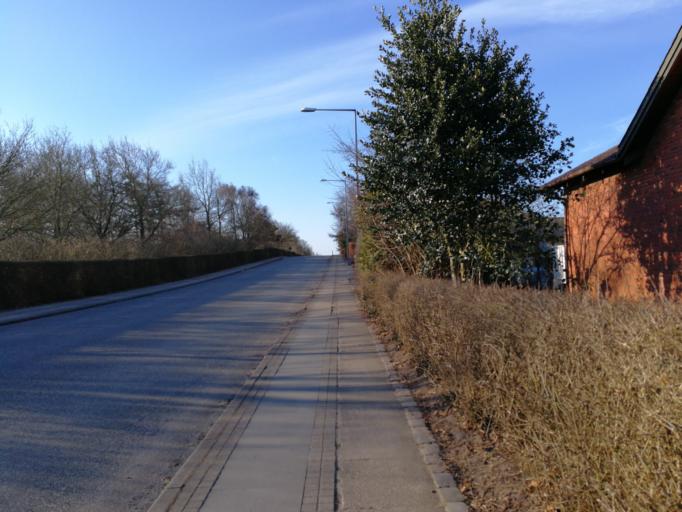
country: DK
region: North Denmark
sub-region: Alborg Kommune
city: Gistrup
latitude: 57.0344
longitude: 9.9663
